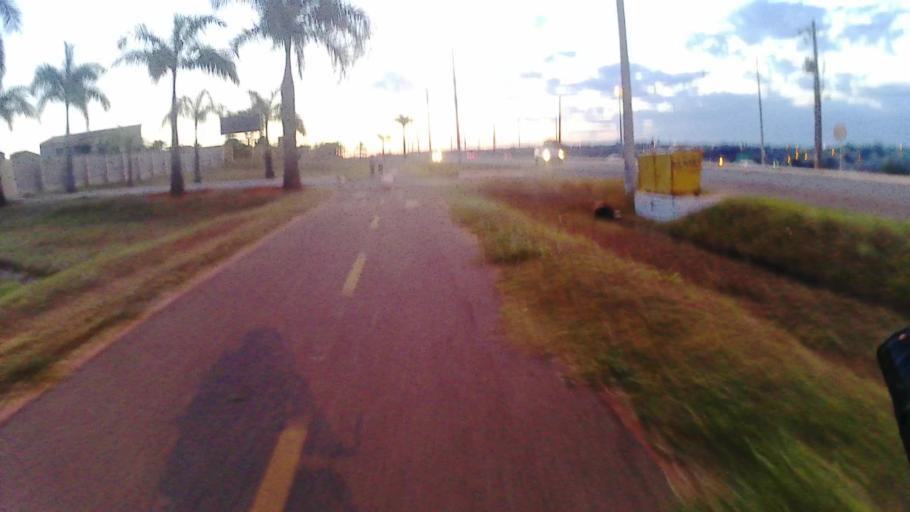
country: BR
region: Federal District
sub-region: Brasilia
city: Brasilia
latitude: -15.8677
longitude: -47.9883
